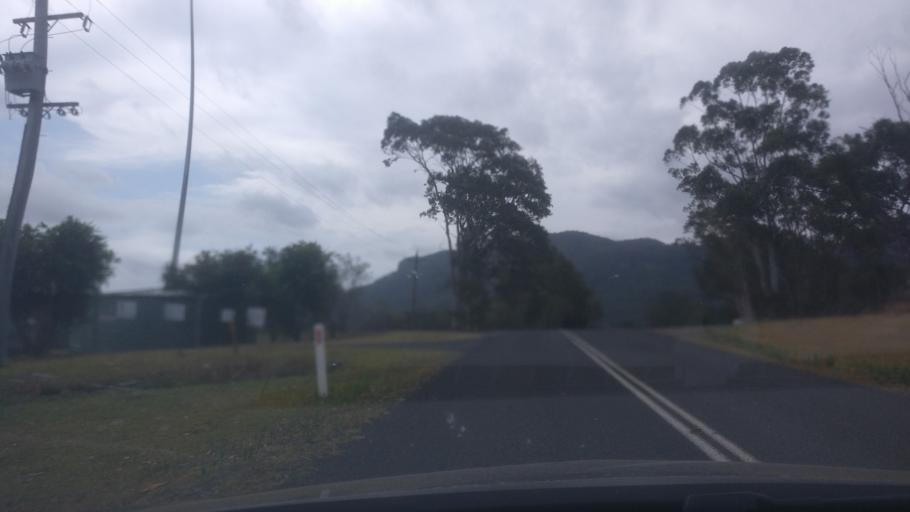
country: AU
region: New South Wales
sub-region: Shoalhaven Shire
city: Kangaroo Valley
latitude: -34.7246
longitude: 150.4804
